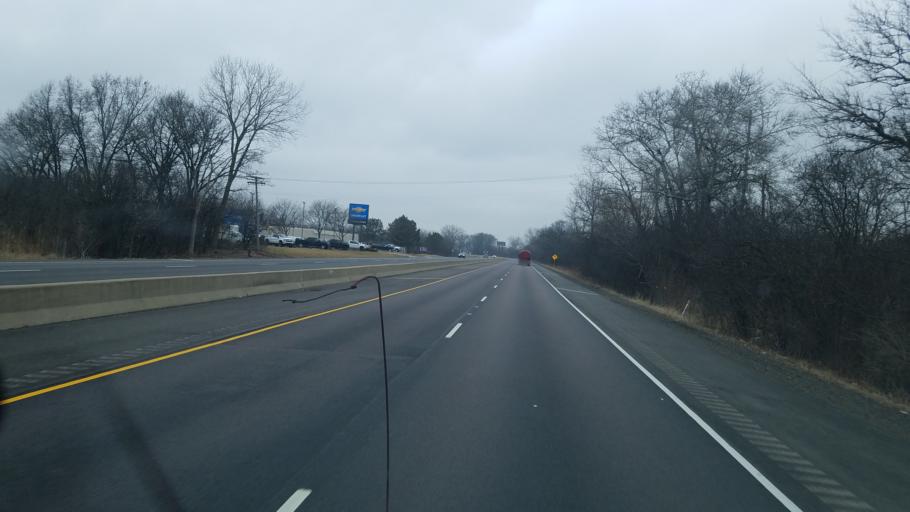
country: US
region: Illinois
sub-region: Lake County
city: Lake Forest
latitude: 42.2681
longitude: -87.8643
